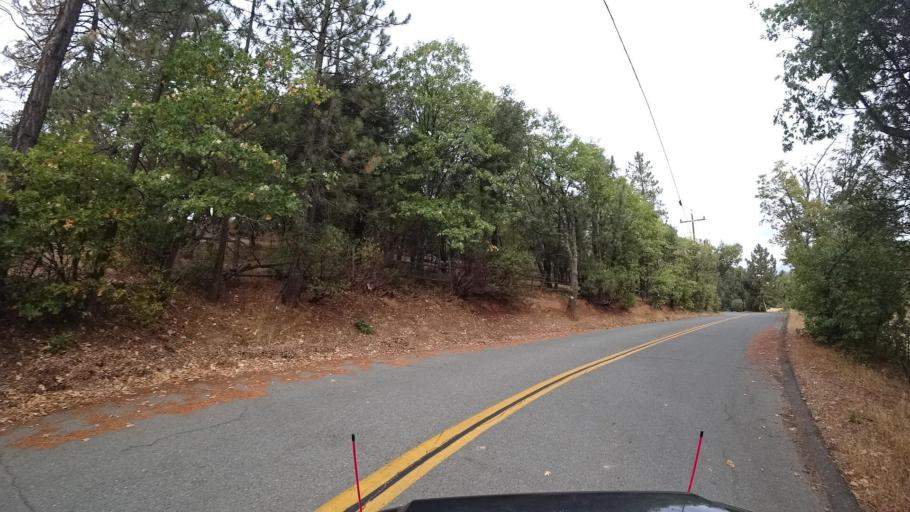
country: US
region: California
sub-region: San Diego County
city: Julian
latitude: 33.0423
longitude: -116.6098
